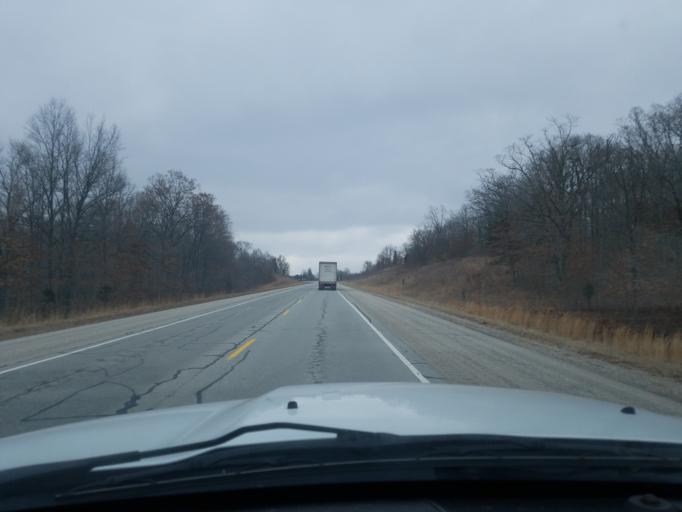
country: US
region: Indiana
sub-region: Perry County
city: Tell City
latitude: 38.0563
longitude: -86.6277
